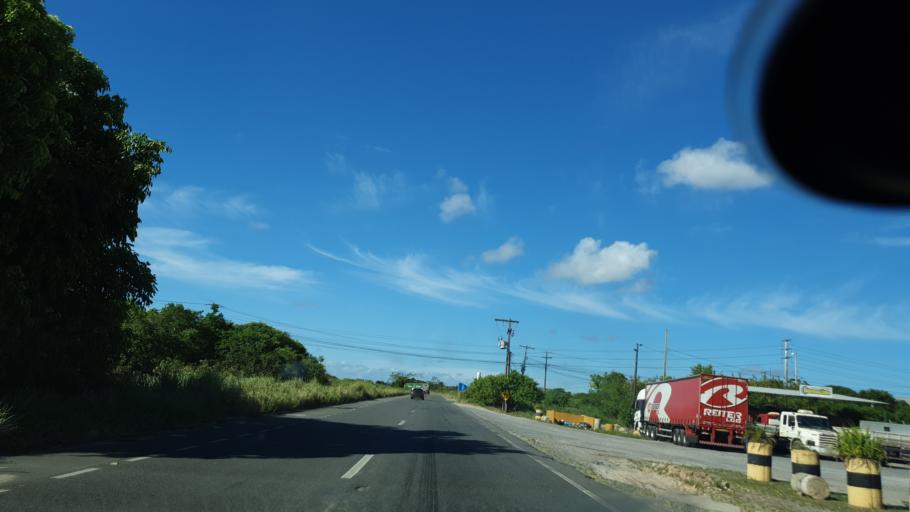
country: BR
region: Bahia
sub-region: Camacari
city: Camacari
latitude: -12.6735
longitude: -38.3003
